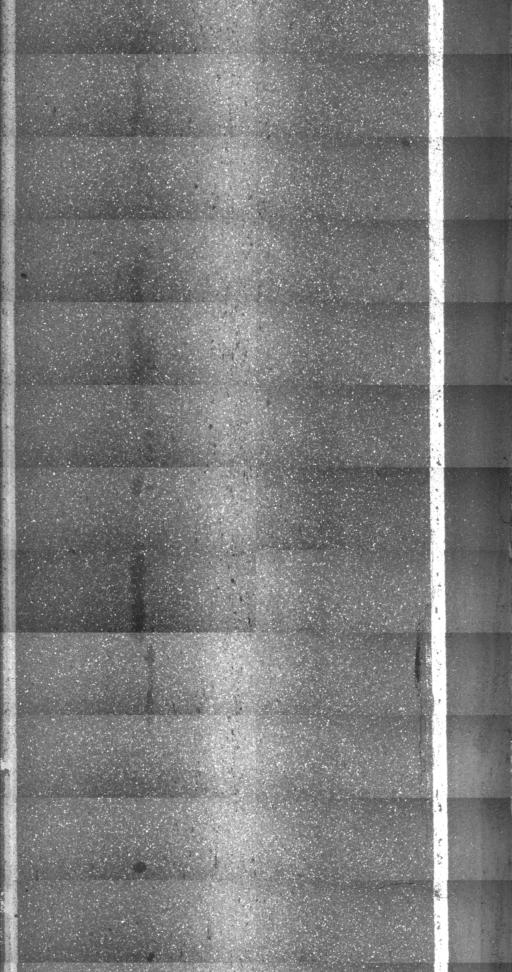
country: US
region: Vermont
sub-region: Orange County
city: Randolph
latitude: 43.8263
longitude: -72.6289
